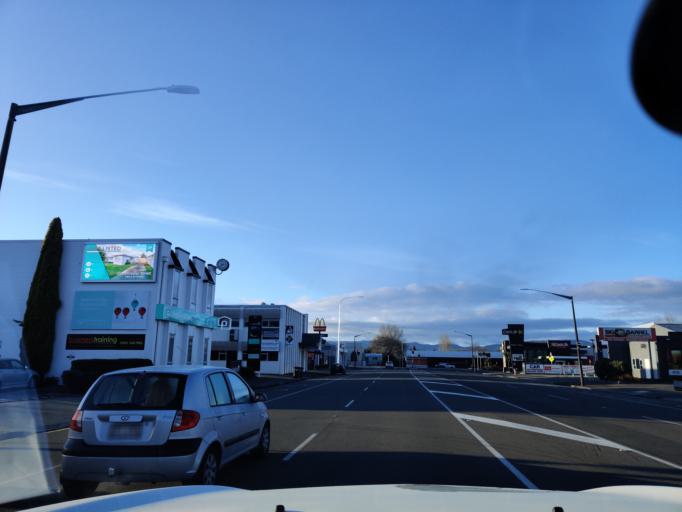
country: NZ
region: Manawatu-Wanganui
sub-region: Palmerston North City
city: Palmerston North
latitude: -40.3564
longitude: 175.6171
